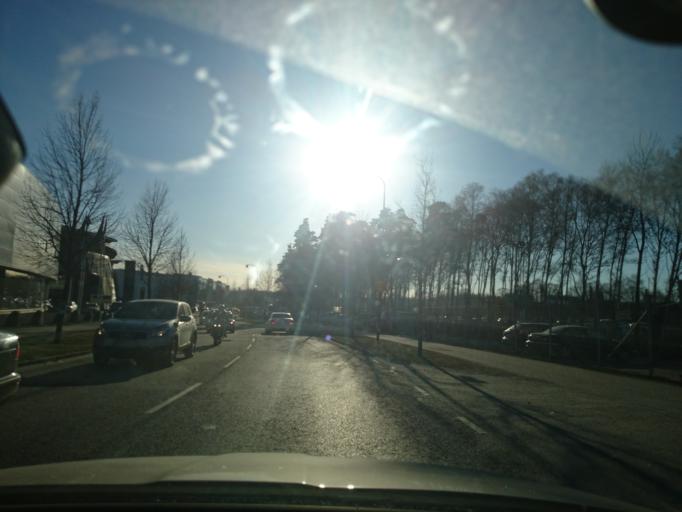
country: SE
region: Stockholm
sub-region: Huddinge Kommun
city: Segeltorp
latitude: 59.2844
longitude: 17.9371
